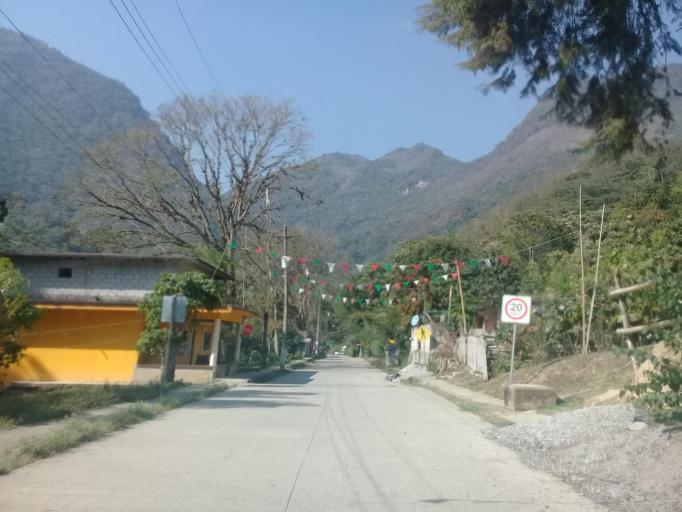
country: MX
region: Veracruz
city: Rafael Delgado
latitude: 18.7823
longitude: -97.0188
